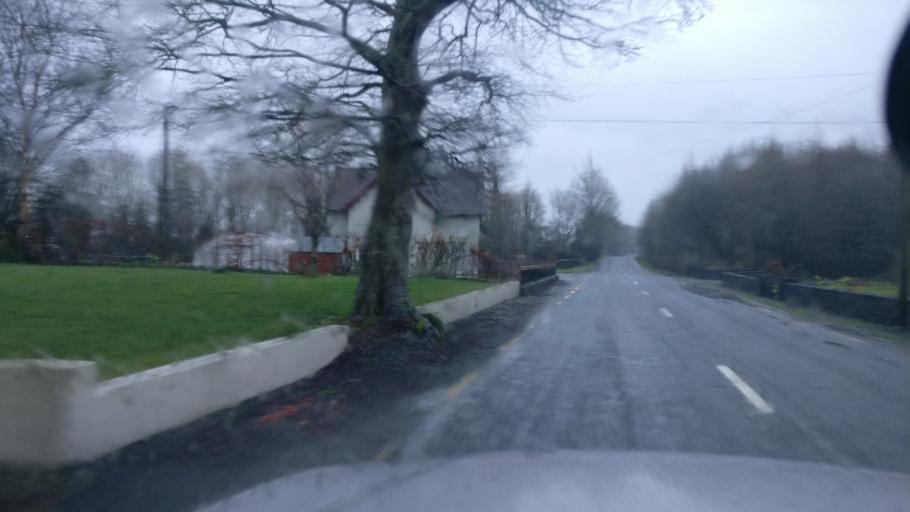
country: IE
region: Connaught
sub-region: County Galway
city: Ballinasloe
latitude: 53.2615
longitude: -8.1873
